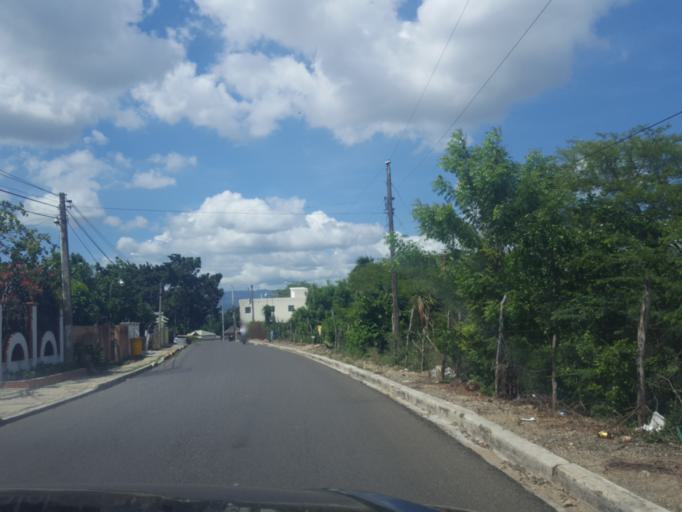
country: DO
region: Santiago
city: Licey al Medio
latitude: 19.3937
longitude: -70.6472
